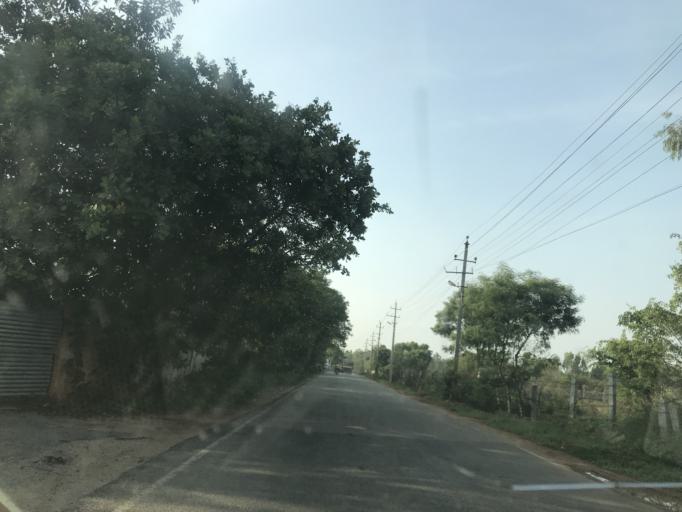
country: IN
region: Karnataka
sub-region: Bangalore Rural
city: Devanhalli
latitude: 13.1964
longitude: 77.6456
